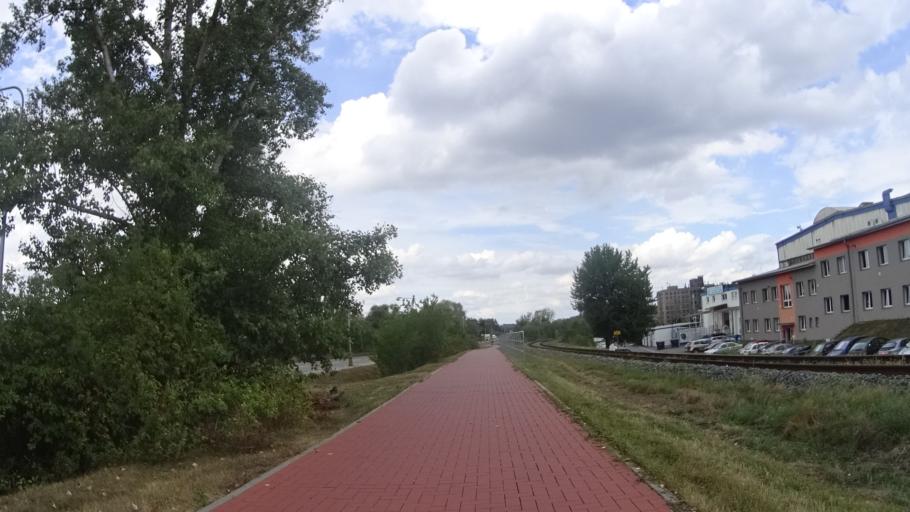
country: CZ
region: Olomoucky
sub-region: Okres Olomouc
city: Olomouc
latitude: 49.6102
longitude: 17.2271
